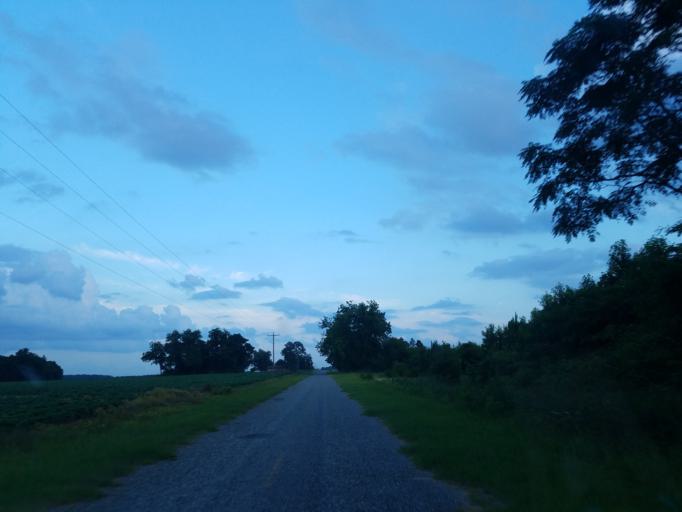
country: US
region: Georgia
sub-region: Dooly County
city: Vienna
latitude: 32.1646
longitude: -83.7316
